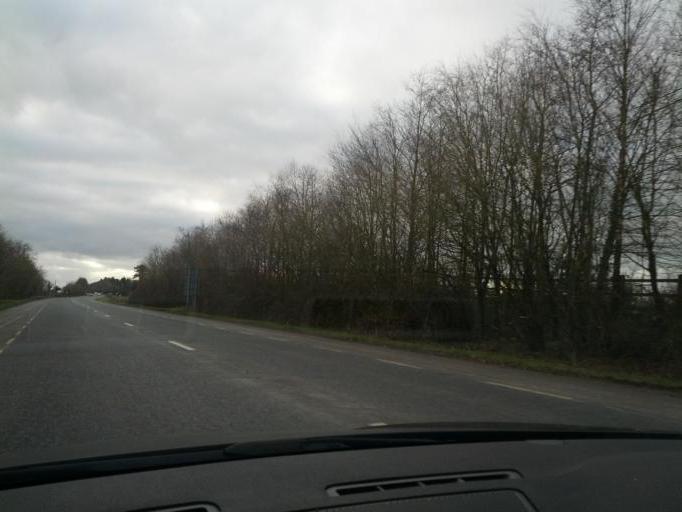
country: IE
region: Leinster
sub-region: An Iarmhi
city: Moate
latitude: 53.3933
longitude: -7.7480
